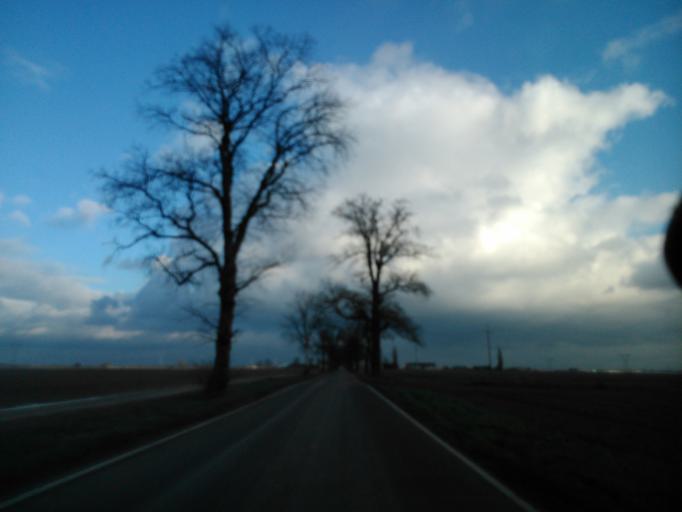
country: PL
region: Masovian Voivodeship
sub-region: Powiat warszawski zachodni
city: Leszno
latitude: 52.2431
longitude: 20.6114
